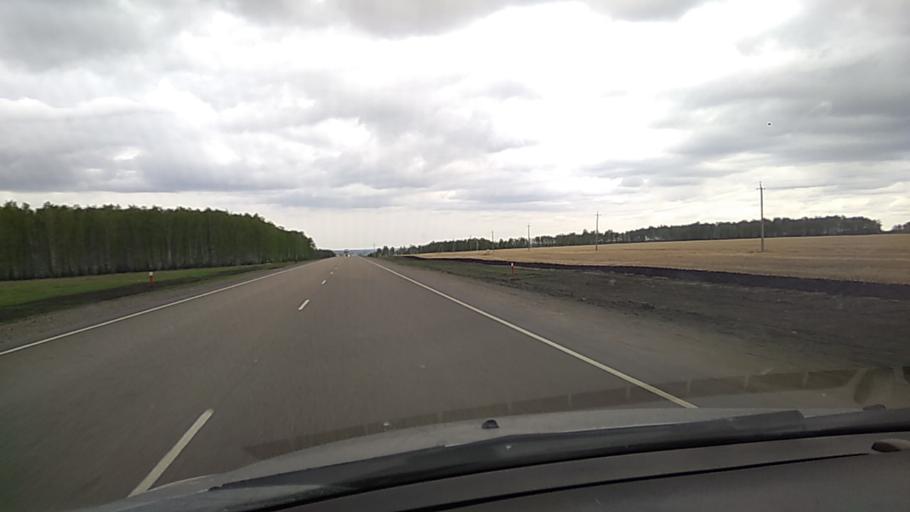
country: RU
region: Kurgan
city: Kataysk
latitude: 56.3075
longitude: 62.5312
